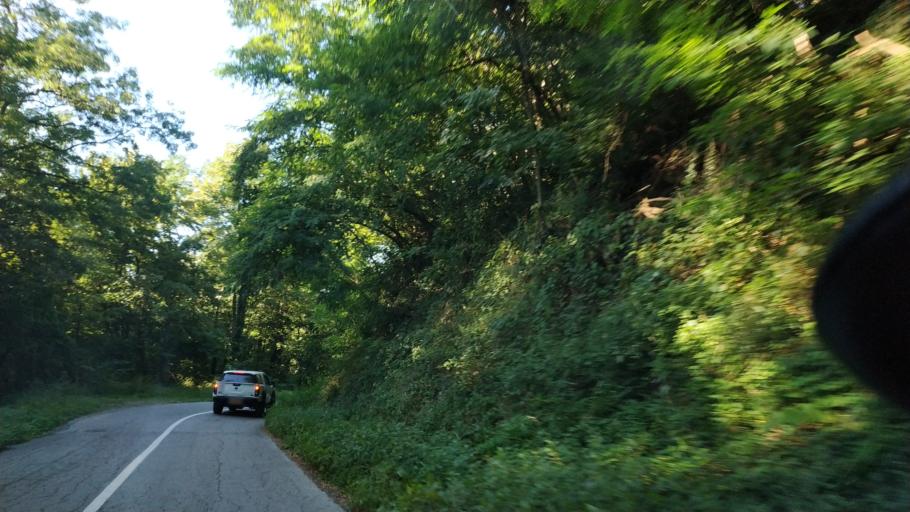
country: RS
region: Central Serbia
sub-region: Rasinski Okrug
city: Krusevac
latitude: 43.4603
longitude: 21.3604
